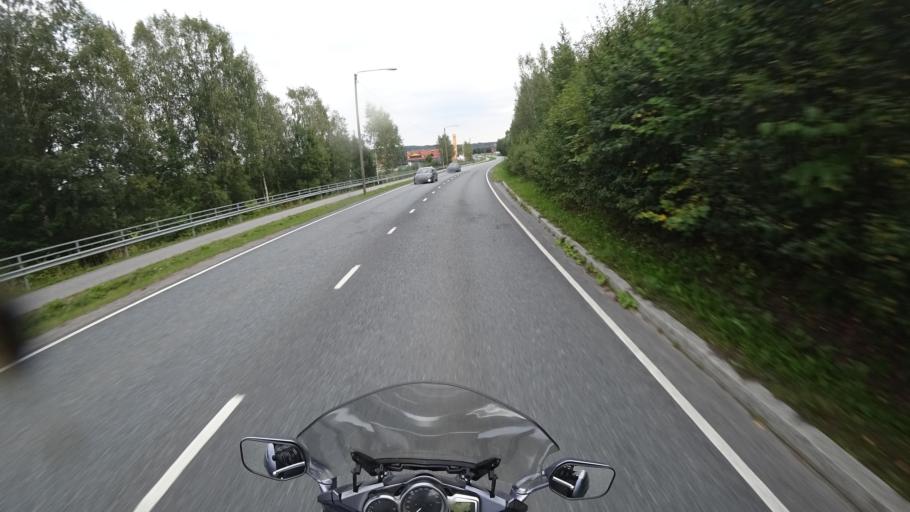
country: FI
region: Uusimaa
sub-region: Raaseporin
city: Karis
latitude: 60.0573
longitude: 23.6441
